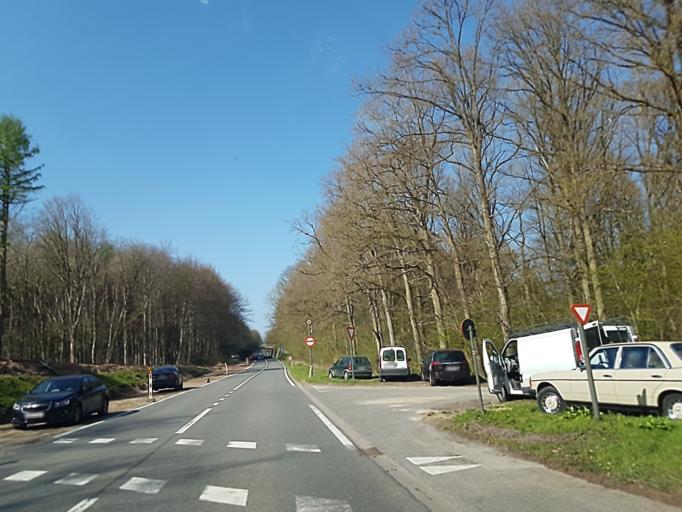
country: BE
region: Wallonia
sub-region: Province du Brabant Wallon
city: Grez-Doiceau
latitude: 50.7959
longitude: 4.7103
